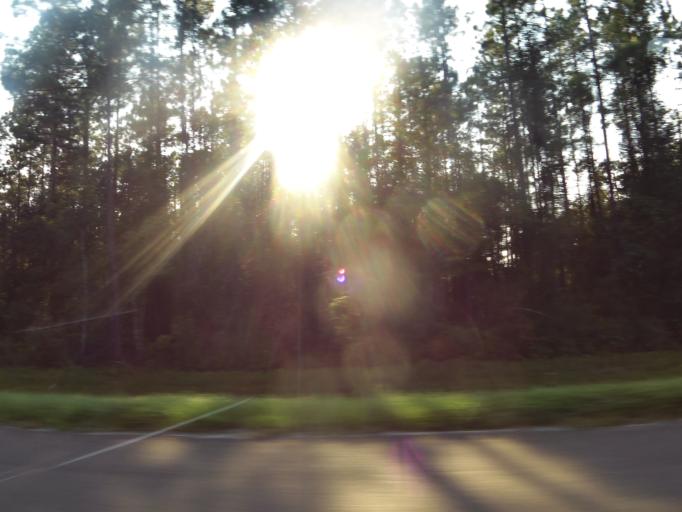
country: US
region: Florida
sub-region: Duval County
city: Baldwin
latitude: 30.3150
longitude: -82.0085
